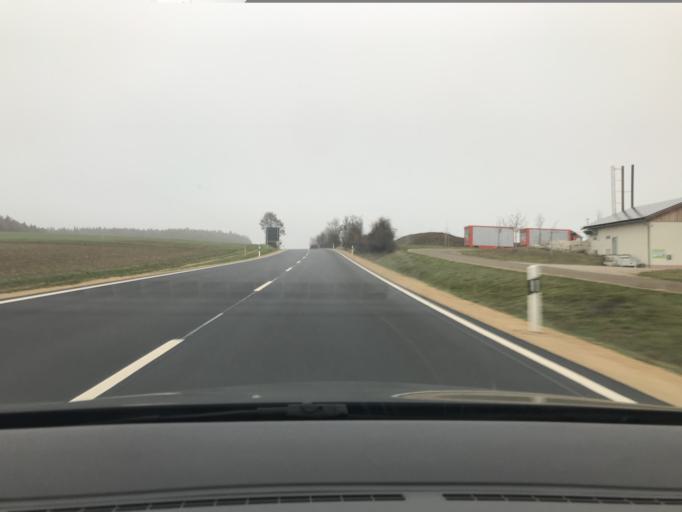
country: DE
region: Bavaria
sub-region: Swabia
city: Fremdingen
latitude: 48.9441
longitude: 10.4586
